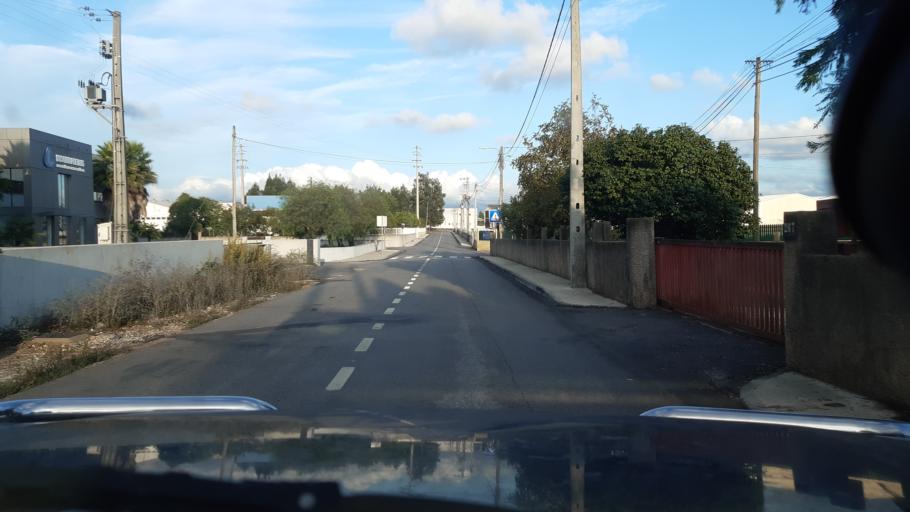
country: PT
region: Aveiro
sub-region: Agueda
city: Agueda
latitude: 40.5819
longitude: -8.4672
